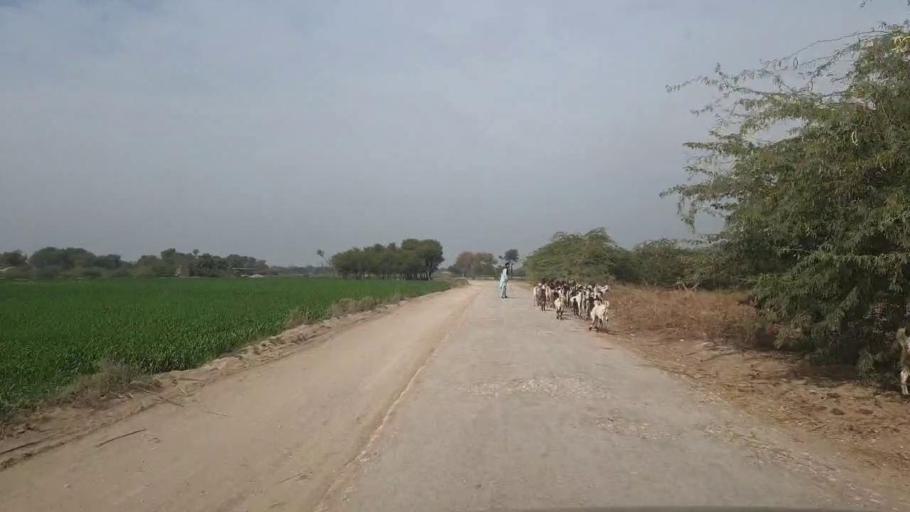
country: PK
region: Sindh
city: Nawabshah
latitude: 26.1117
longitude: 68.4806
